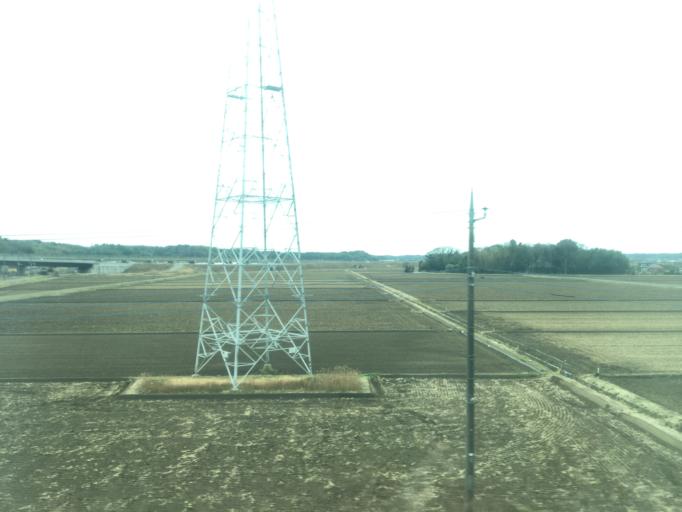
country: JP
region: Chiba
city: Narita
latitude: 35.8030
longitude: 140.2848
